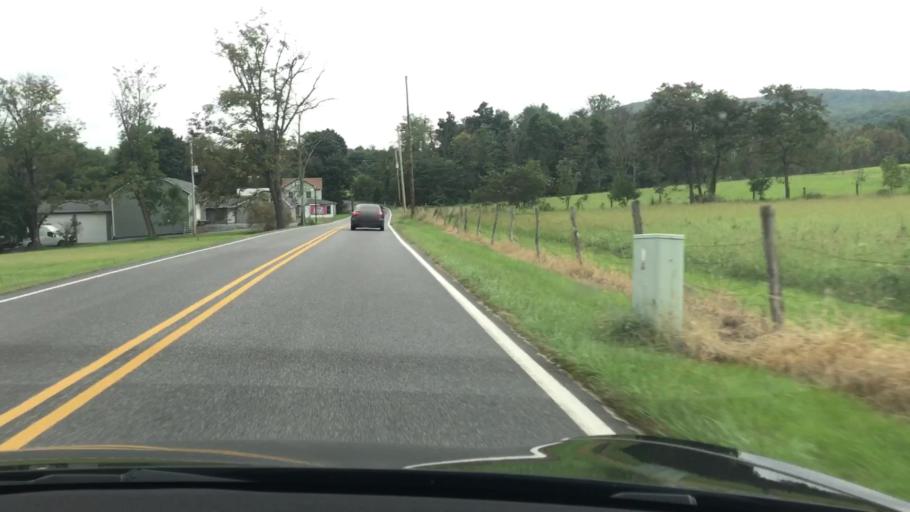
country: US
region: Pennsylvania
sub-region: York County
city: Dillsburg
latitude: 40.0817
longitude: -77.0675
